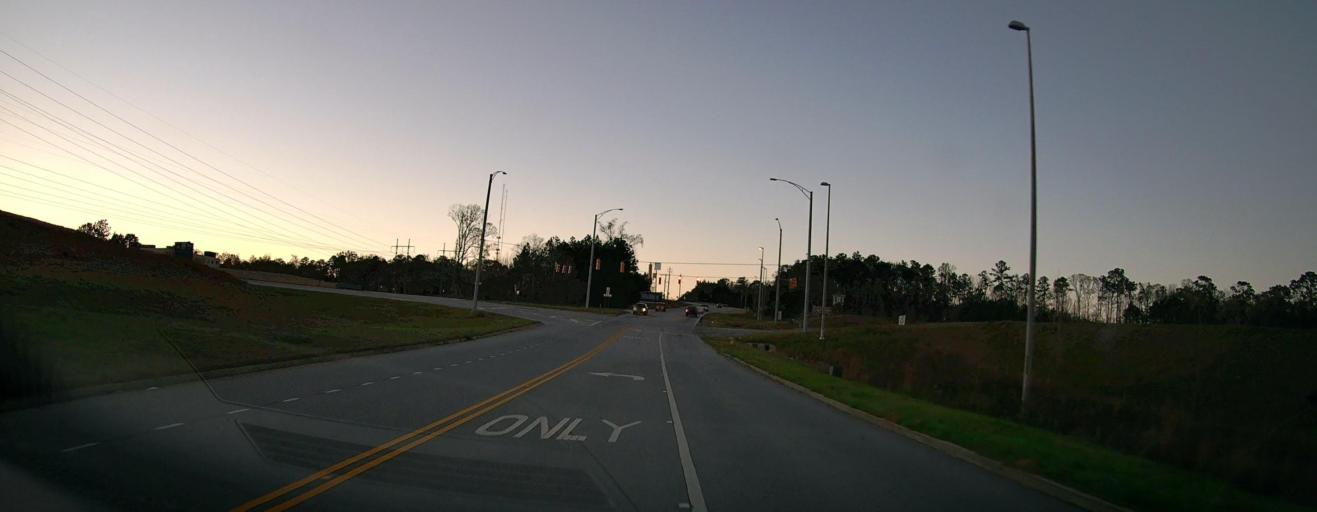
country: US
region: Alabama
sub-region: Russell County
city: Phenix City
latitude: 32.5071
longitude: -85.0041
